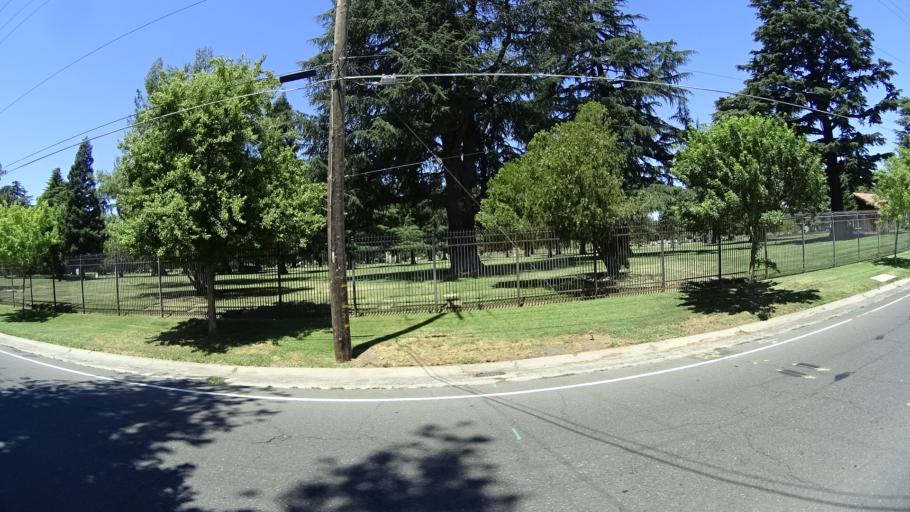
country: US
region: California
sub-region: Sacramento County
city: Sacramento
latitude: 38.5595
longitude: -121.5006
